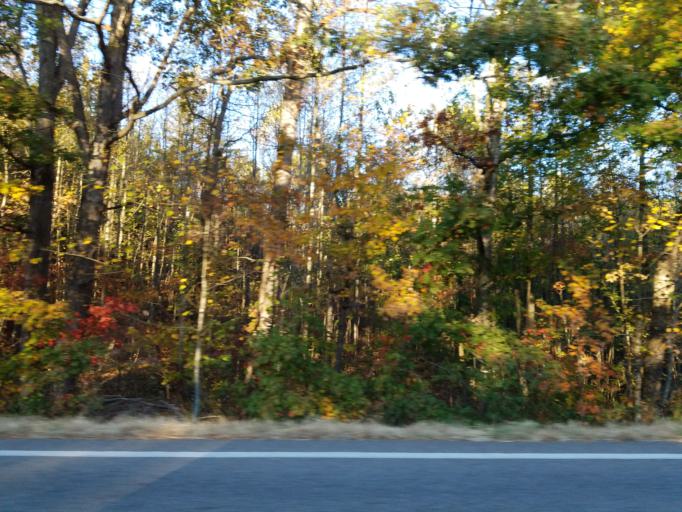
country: US
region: Georgia
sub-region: Pickens County
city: Jasper
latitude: 34.5412
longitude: -84.2679
